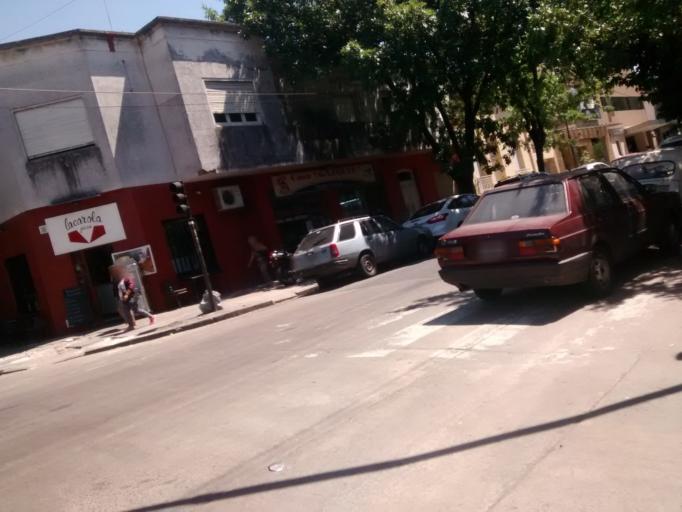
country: AR
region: Buenos Aires
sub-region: Partido de La Plata
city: La Plata
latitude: -34.9053
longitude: -57.9534
